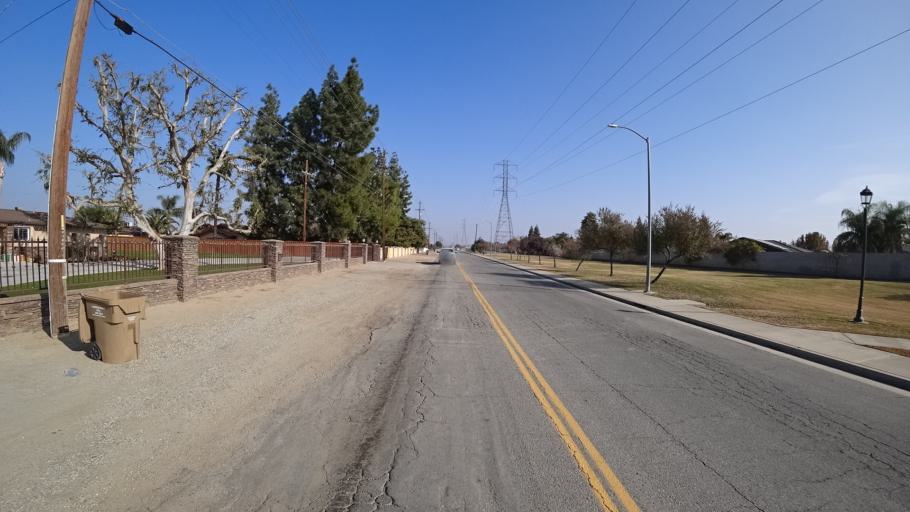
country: US
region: California
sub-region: Kern County
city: Greenacres
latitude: 35.3978
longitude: -119.0715
